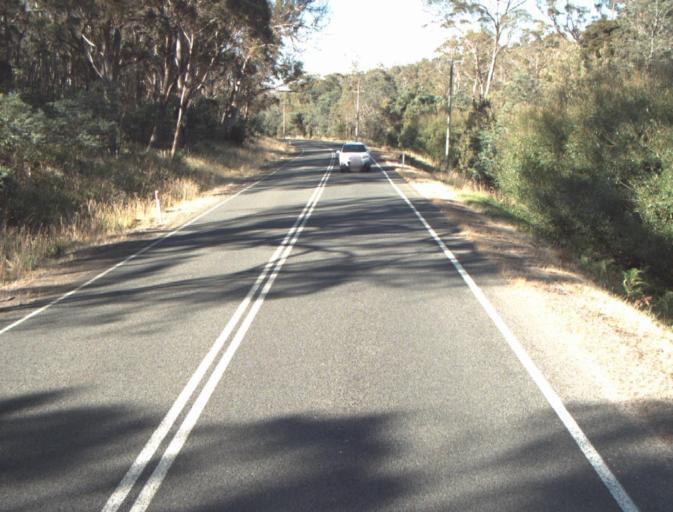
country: AU
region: Tasmania
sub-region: Launceston
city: Newstead
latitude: -41.4204
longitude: 147.2569
